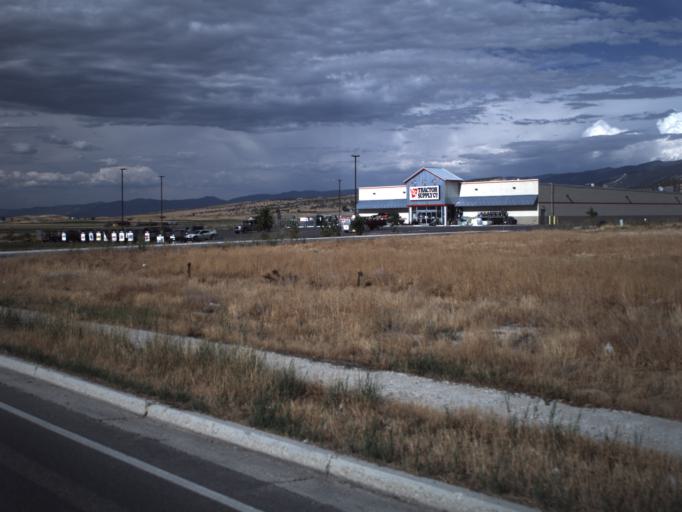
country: US
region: Utah
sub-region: Sanpete County
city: Ephraim
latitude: 39.3742
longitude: -111.5870
